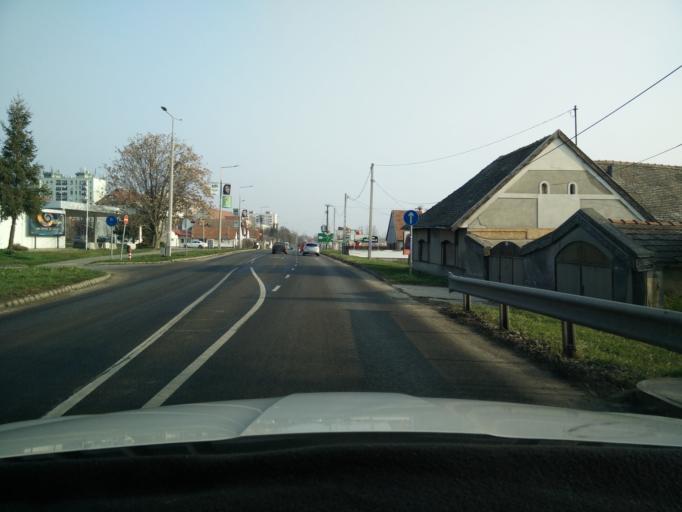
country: HU
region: Tolna
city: Szekszard
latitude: 46.3284
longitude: 18.6992
